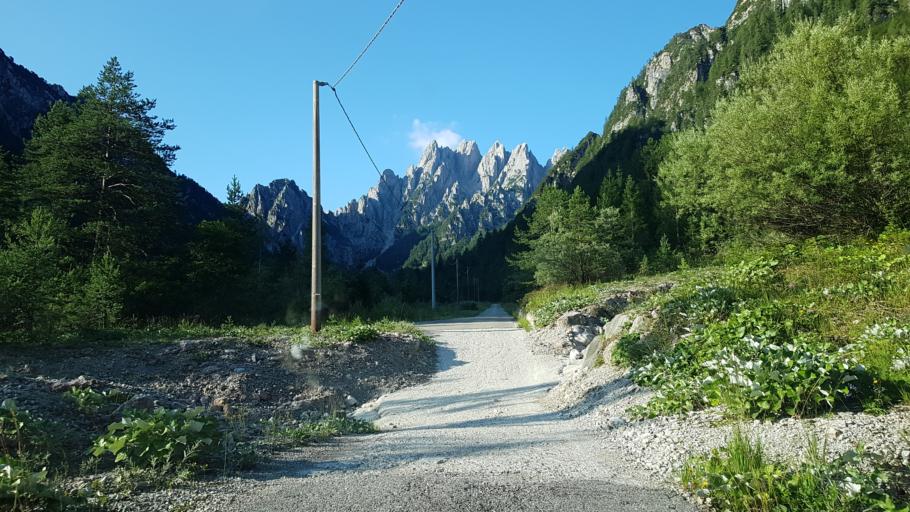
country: IT
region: Friuli Venezia Giulia
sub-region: Provincia di Udine
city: Pontebba
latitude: 46.5006
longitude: 13.2540
